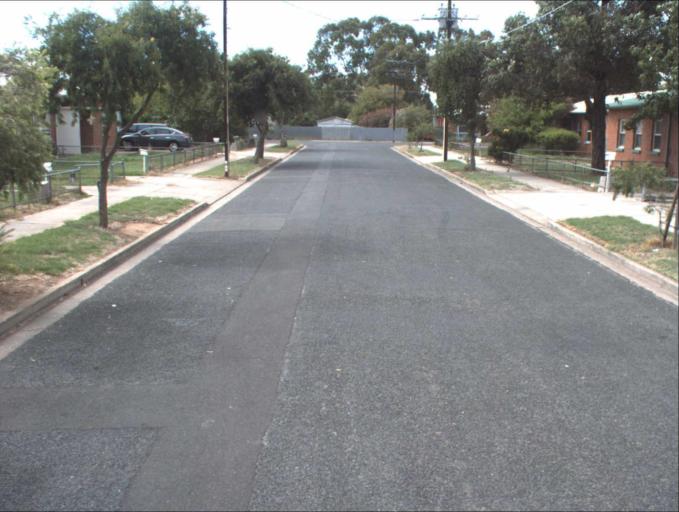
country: AU
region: South Australia
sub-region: Port Adelaide Enfield
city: Blair Athol
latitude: -34.8586
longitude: 138.5886
